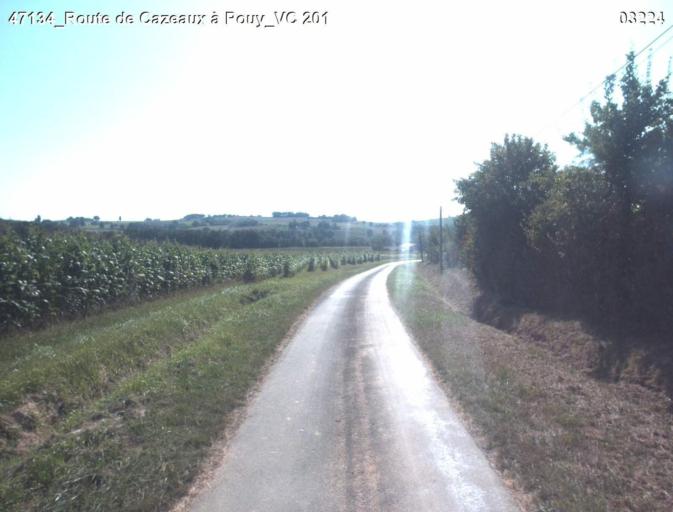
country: FR
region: Aquitaine
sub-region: Departement du Lot-et-Garonne
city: Mezin
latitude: 44.0278
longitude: 0.3095
